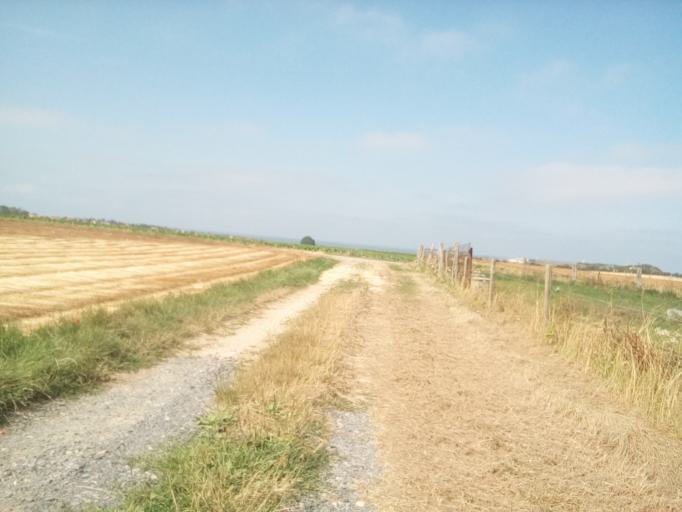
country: FR
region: Lower Normandy
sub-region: Departement du Calvados
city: Bernieres-sur-Mer
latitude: 49.3153
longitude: -0.4389
